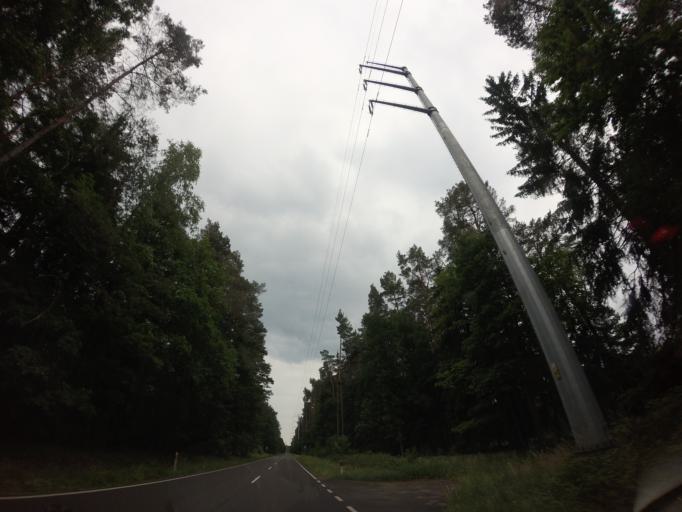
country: PL
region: West Pomeranian Voivodeship
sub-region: Powiat drawski
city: Czaplinek
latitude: 53.4945
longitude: 16.2249
